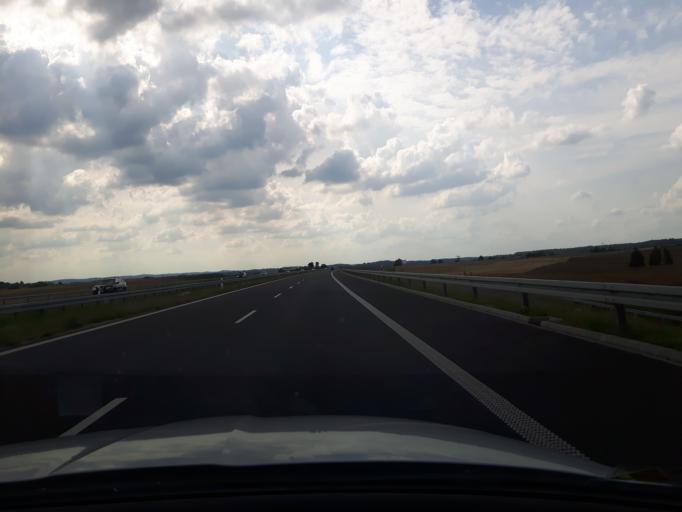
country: PL
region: Warmian-Masurian Voivodeship
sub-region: Powiat ostrodzki
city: Gierzwald
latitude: 53.5924
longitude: 20.1108
